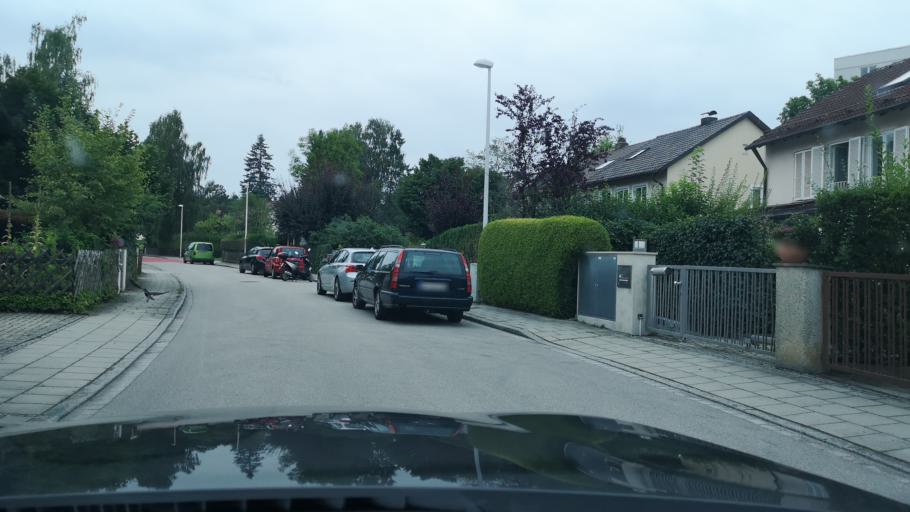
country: DE
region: Bavaria
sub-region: Upper Bavaria
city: Unterhaching
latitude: 48.0808
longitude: 11.6024
